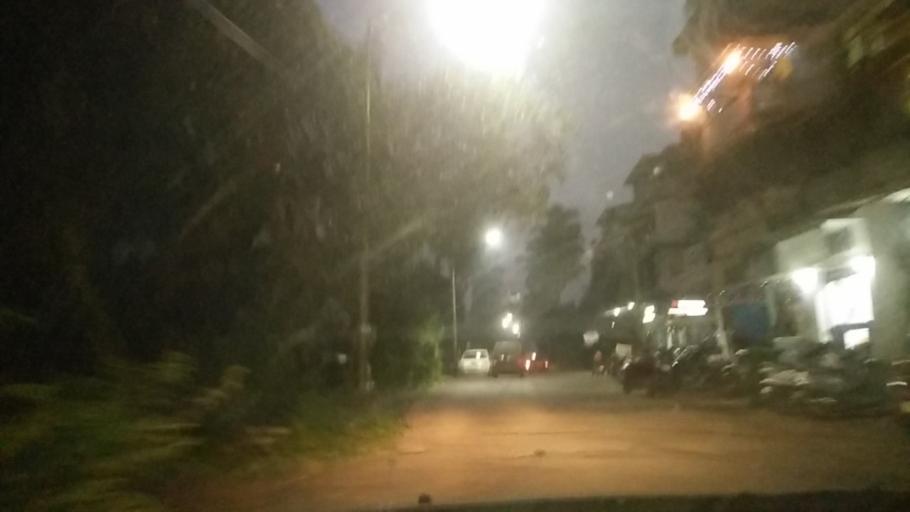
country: IN
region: Goa
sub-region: South Goa
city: Madgaon
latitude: 15.2641
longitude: 73.9648
